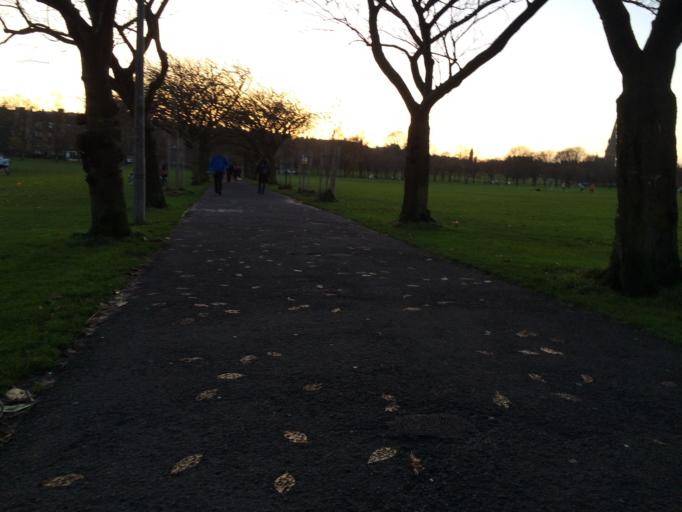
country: GB
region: Scotland
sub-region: Edinburgh
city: Edinburgh
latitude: 55.9420
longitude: -3.1923
